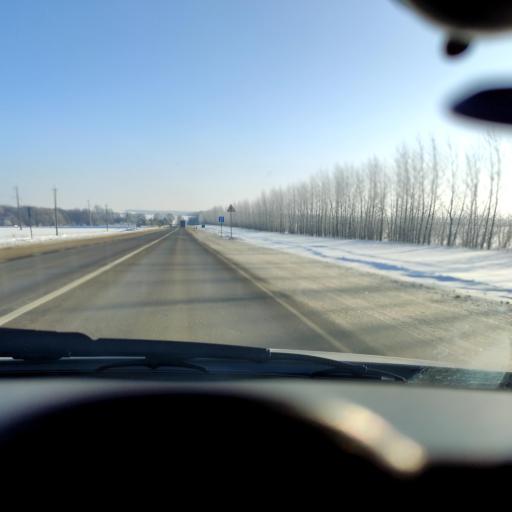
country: RU
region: Kursk
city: Tim
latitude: 51.6532
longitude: 36.9436
